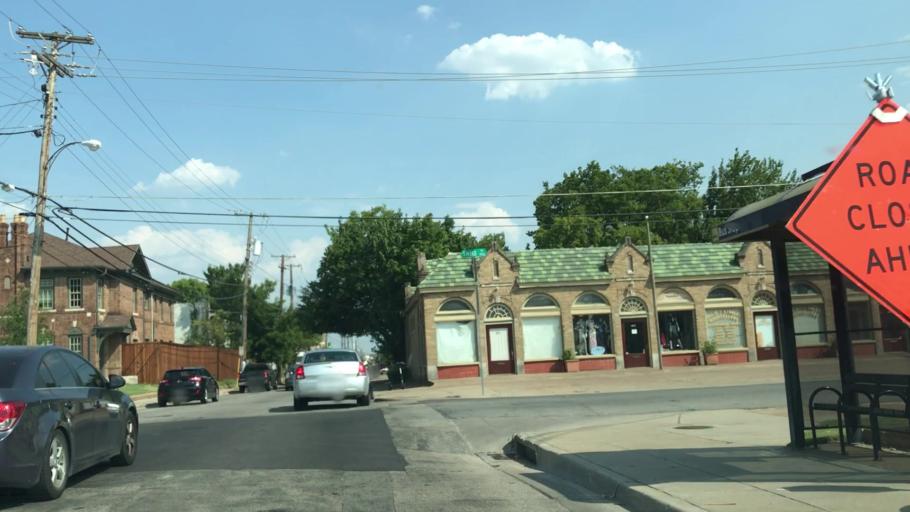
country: US
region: Texas
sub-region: Dallas County
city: Dallas
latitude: 32.7952
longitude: -96.7783
